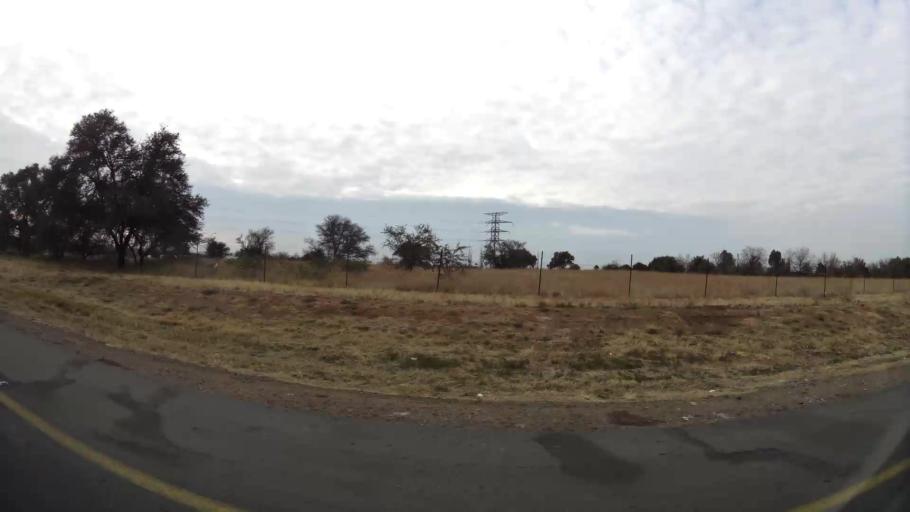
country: ZA
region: Orange Free State
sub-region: Mangaung Metropolitan Municipality
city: Bloemfontein
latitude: -29.1277
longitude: 26.1645
